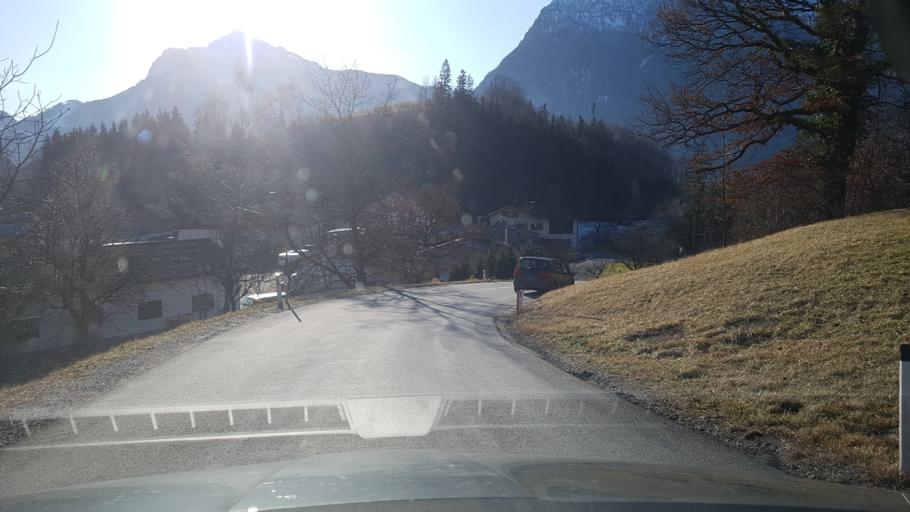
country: AT
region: Salzburg
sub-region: Politischer Bezirk Hallein
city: Golling an der Salzach
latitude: 47.6183
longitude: 13.1734
